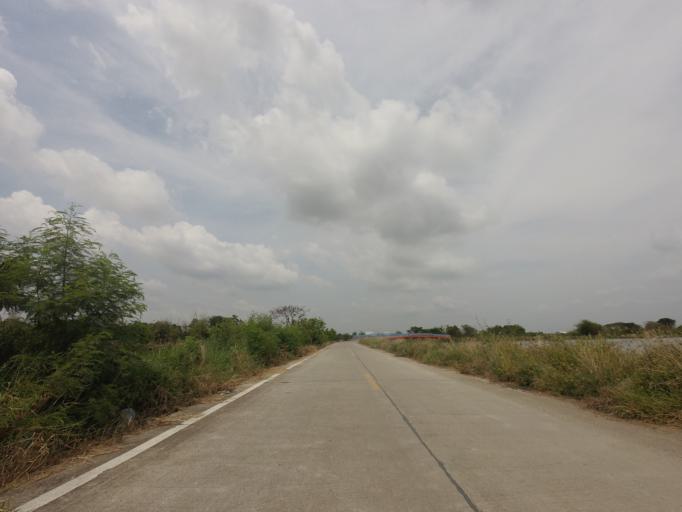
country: TH
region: Bangkok
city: Lat Krabang
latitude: 13.6802
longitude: 100.7707
